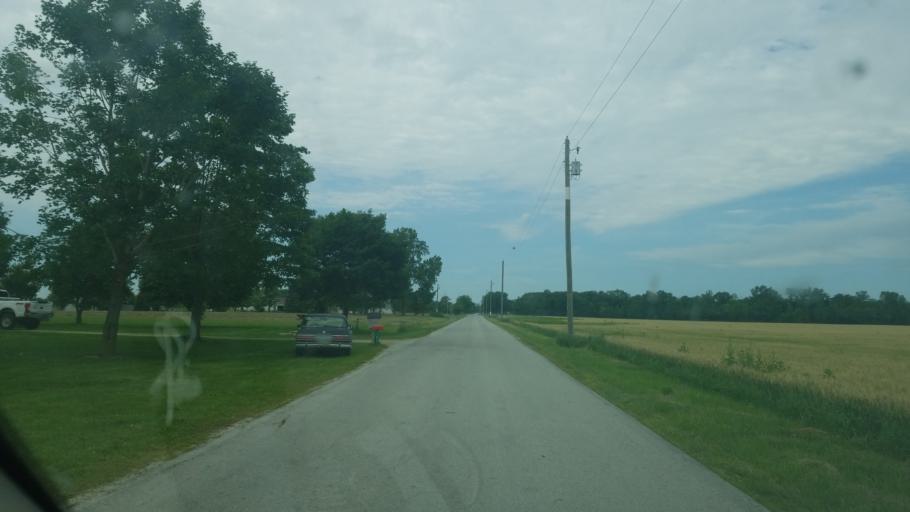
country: US
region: Ohio
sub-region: Wood County
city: North Baltimore
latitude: 41.2220
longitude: -83.6241
